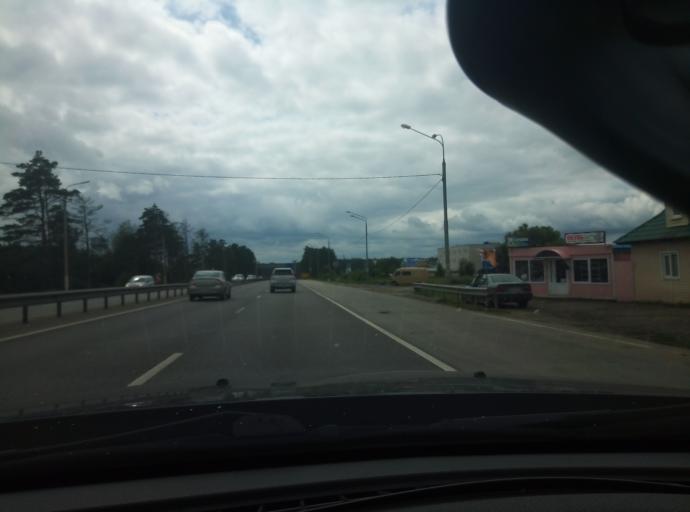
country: RU
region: Kaluga
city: Obninsk
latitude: 55.0745
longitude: 36.6270
